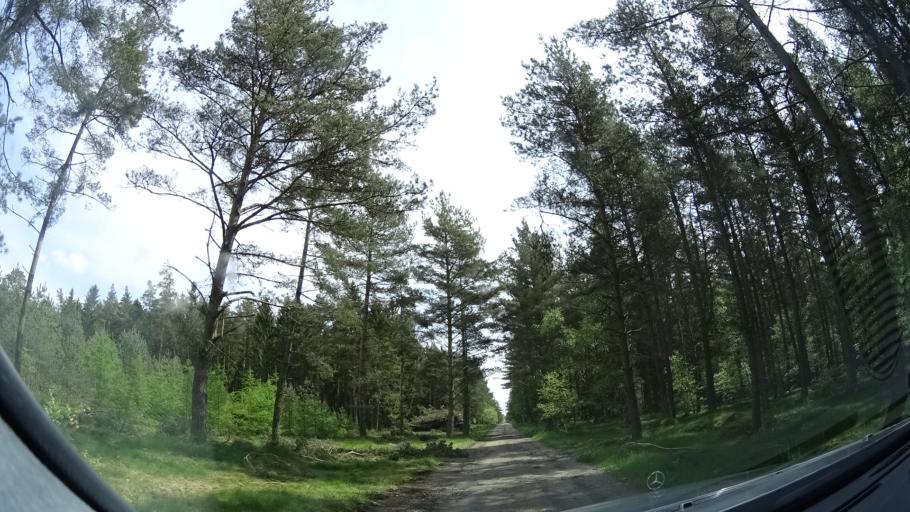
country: SE
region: Skane
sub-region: Sjobo Kommun
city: Sjoebo
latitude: 55.6690
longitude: 13.6436
